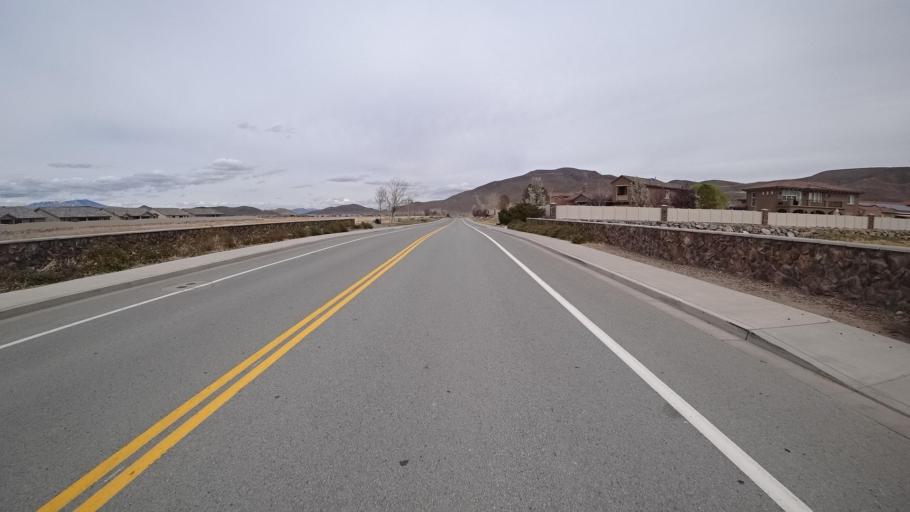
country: US
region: Nevada
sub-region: Washoe County
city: Sparks
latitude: 39.4342
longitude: -119.7173
